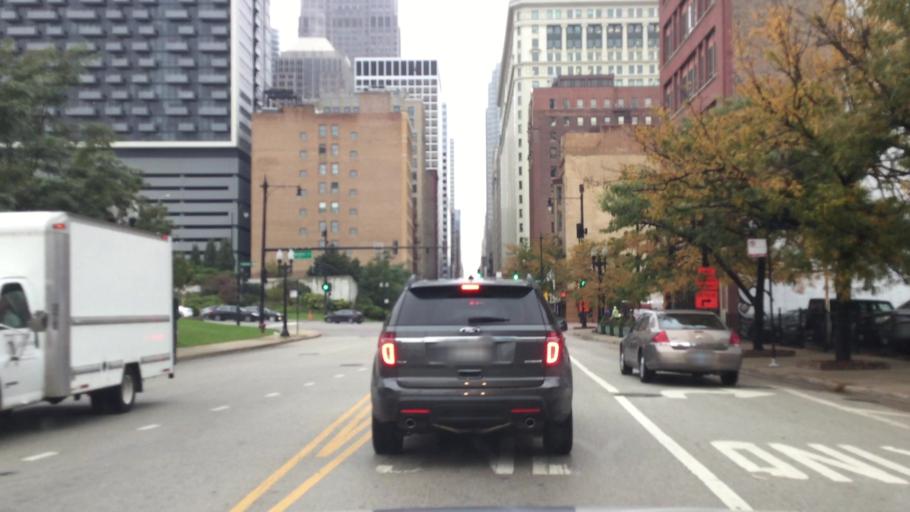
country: US
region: Illinois
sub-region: Cook County
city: Chicago
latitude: 41.8749
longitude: -87.6338
